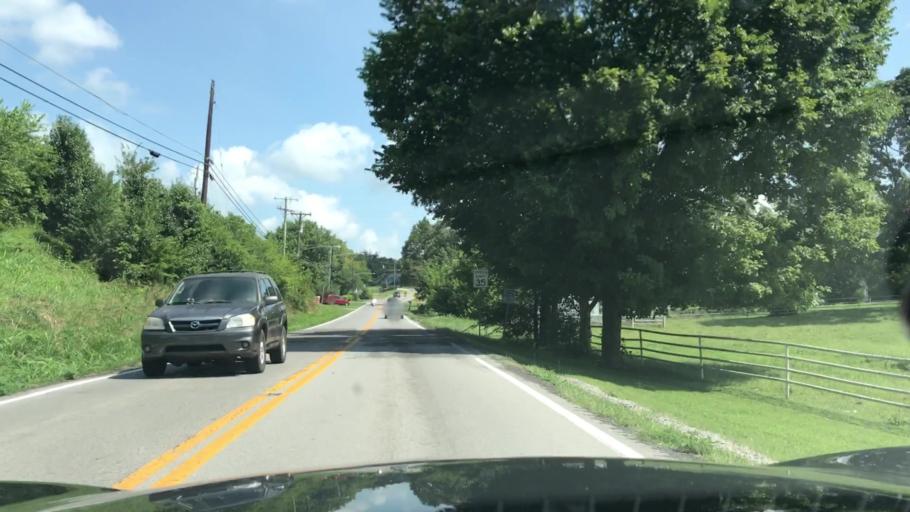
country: US
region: Kentucky
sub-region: Adair County
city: Columbia
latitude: 37.0921
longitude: -85.3173
